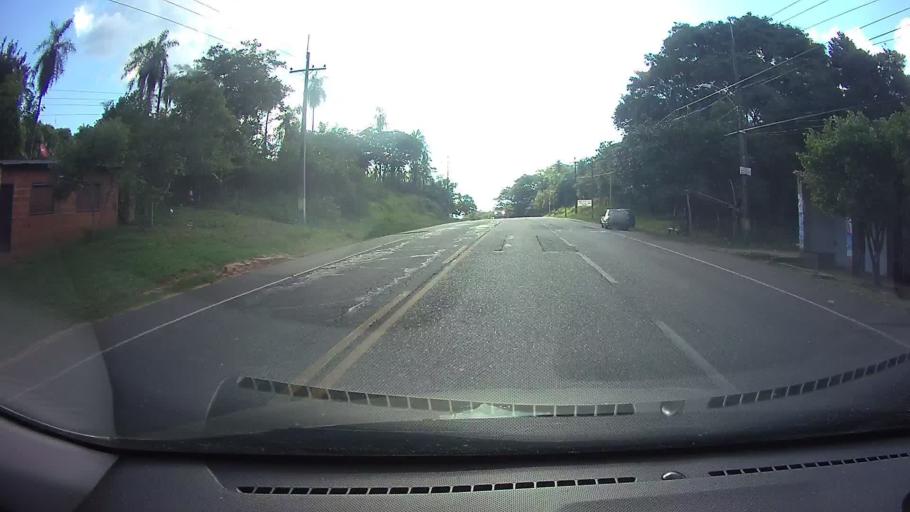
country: PY
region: Cordillera
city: Caacupe
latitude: -25.3879
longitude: -57.0931
